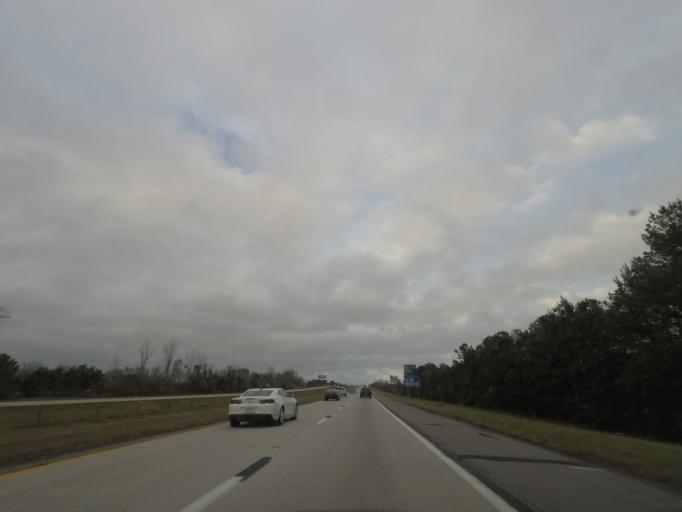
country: US
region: South Carolina
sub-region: Dorchester County
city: Saint George
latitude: 33.1890
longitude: -80.6080
